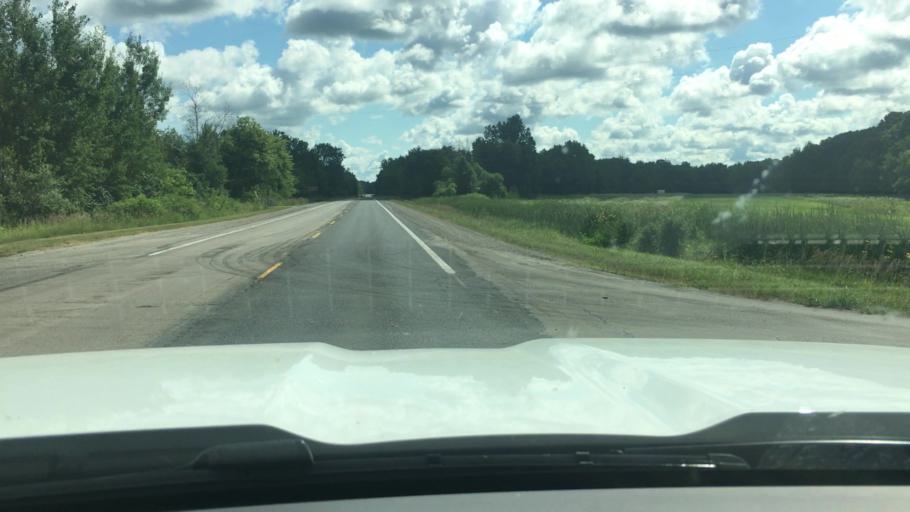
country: US
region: Michigan
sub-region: Clinton County
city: Ovid
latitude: 43.1817
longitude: -84.3460
